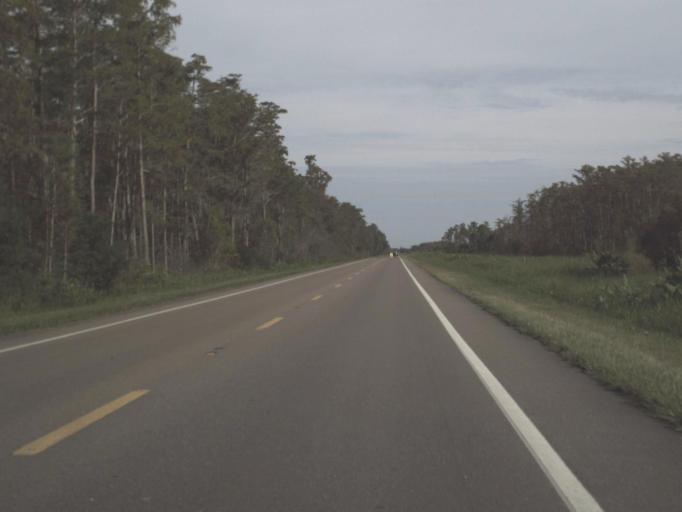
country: US
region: Florida
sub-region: Lee County
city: Olga
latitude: 26.9254
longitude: -81.7605
